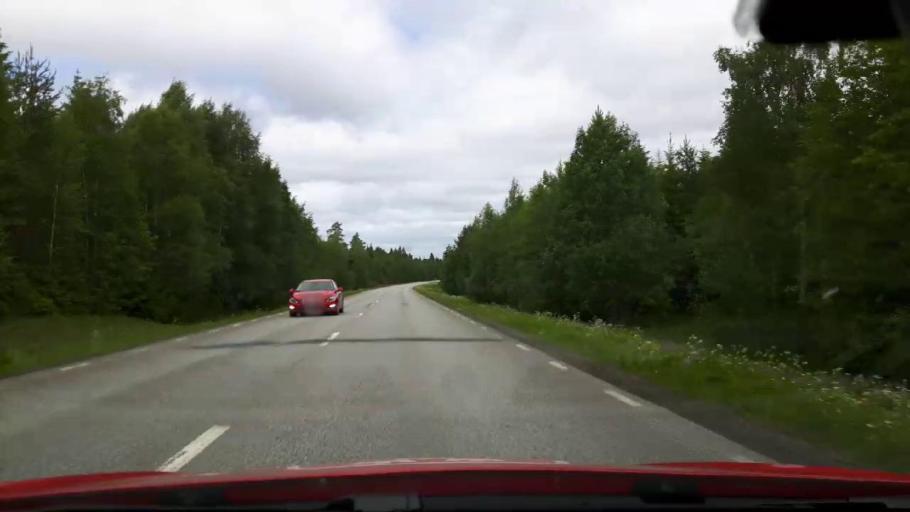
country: SE
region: Jaemtland
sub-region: Krokoms Kommun
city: Krokom
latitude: 63.3731
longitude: 14.5067
